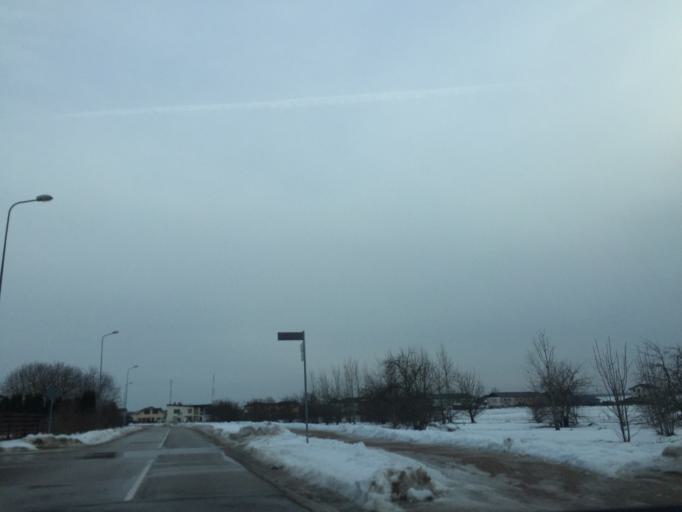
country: LV
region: Ikskile
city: Ikskile
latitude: 56.8397
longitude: 24.4739
